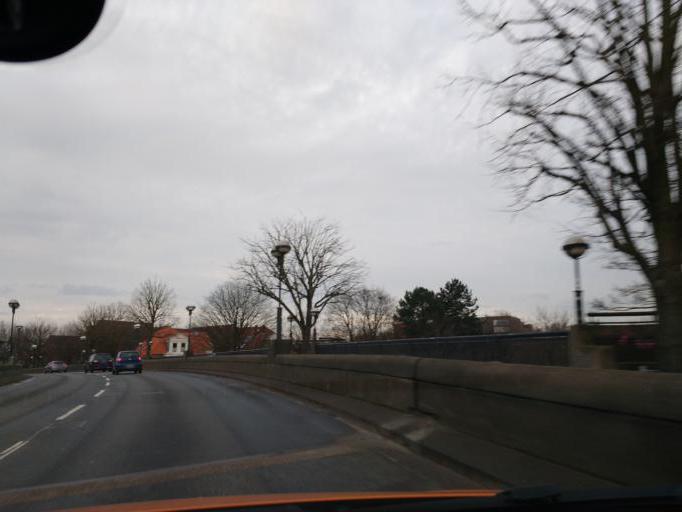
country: DE
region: Lower Saxony
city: Oldenburg
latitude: 53.1384
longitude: 8.2256
